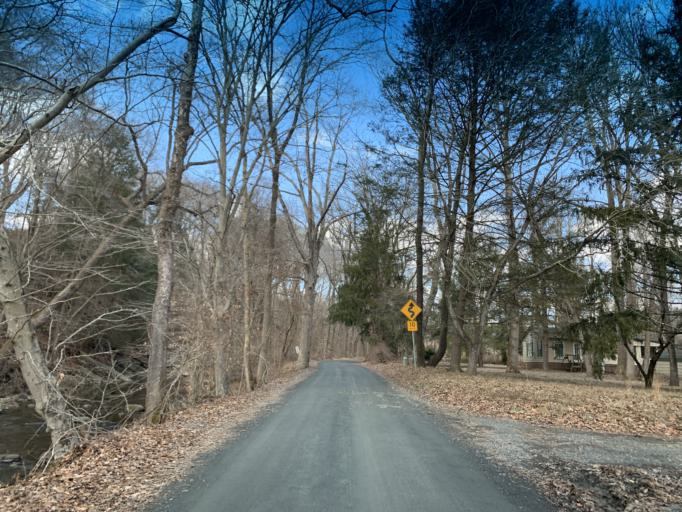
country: US
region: Maryland
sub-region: Harford County
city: Riverside
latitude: 39.5036
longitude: -76.2585
